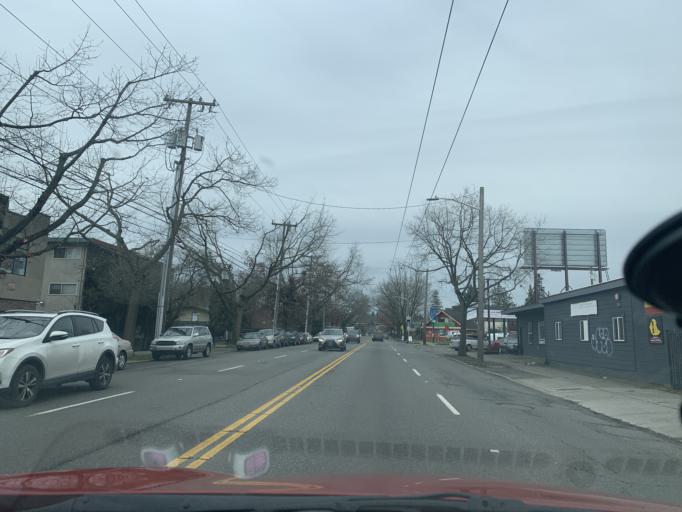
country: US
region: Washington
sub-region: King County
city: Bryn Mawr-Skyway
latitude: 47.5287
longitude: -122.2700
